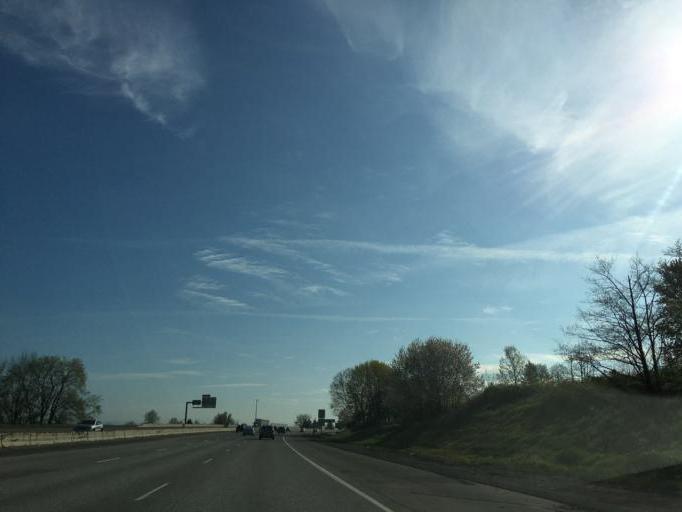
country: US
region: Oregon
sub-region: Multnomah County
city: Fairview
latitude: 45.5409
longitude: -122.4381
